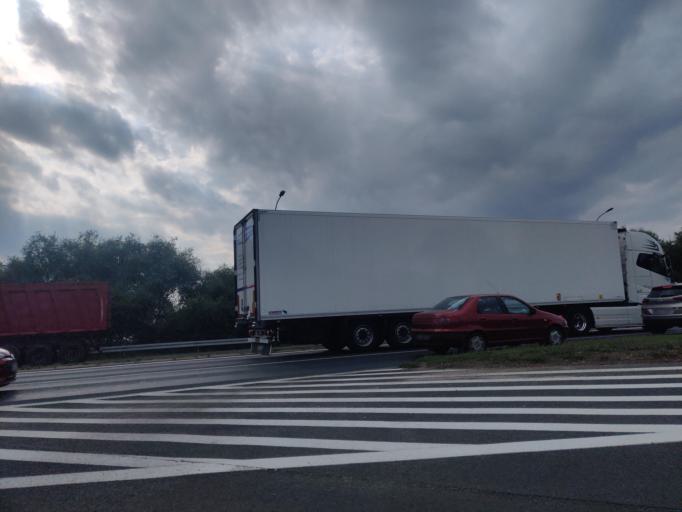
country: PL
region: Greater Poland Voivodeship
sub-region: Konin
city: Konin
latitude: 52.2227
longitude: 18.2514
